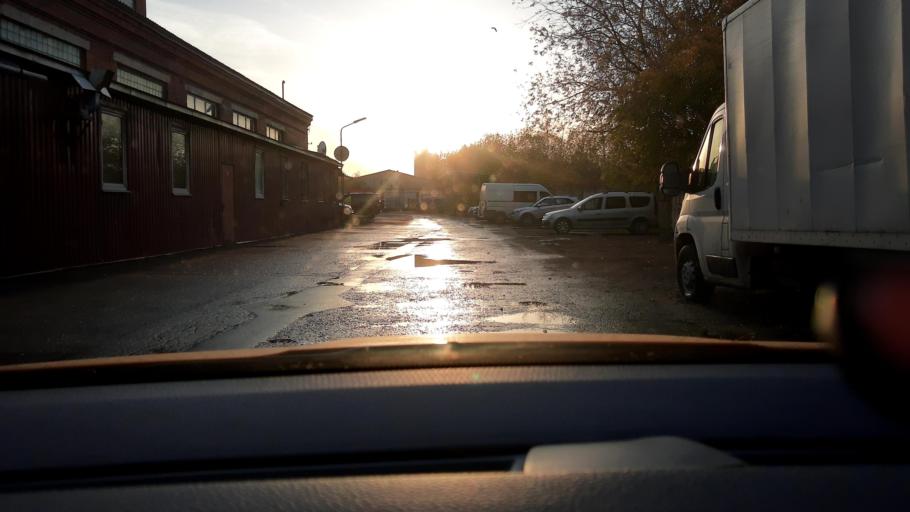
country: RU
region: Moscow
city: Ochakovo-Matveyevskoye
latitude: 55.7052
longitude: 37.4453
